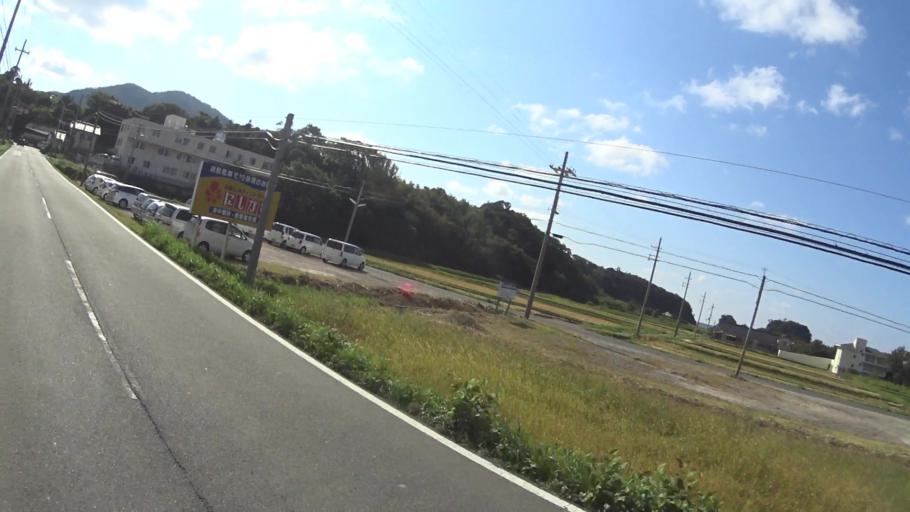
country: JP
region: Kyoto
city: Miyazu
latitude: 35.7552
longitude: 135.1730
